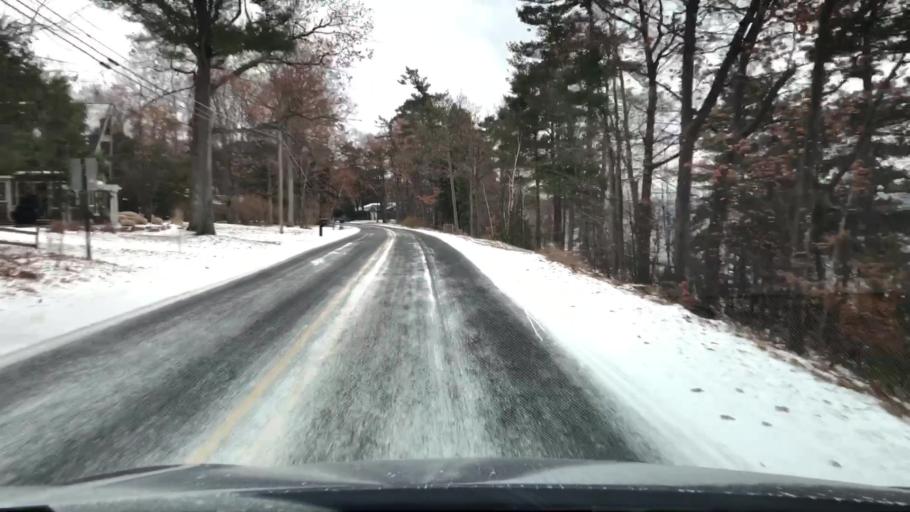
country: US
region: Michigan
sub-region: Grand Traverse County
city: Traverse City
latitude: 44.8293
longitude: -85.5653
